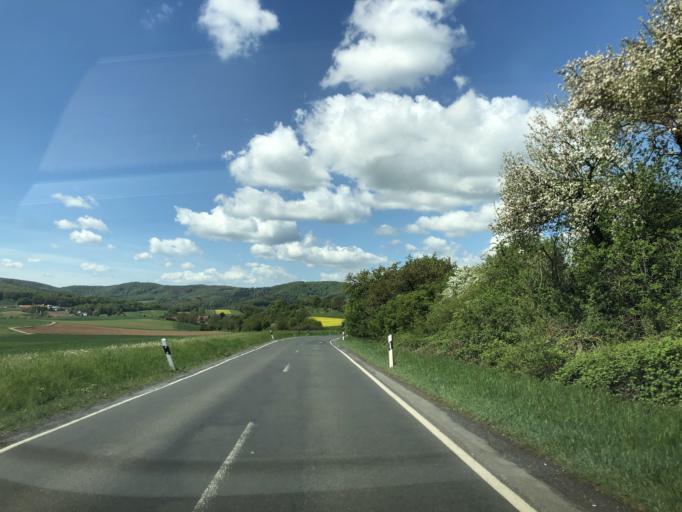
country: DE
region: Hesse
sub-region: Regierungsbezirk Kassel
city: Bad Sooden-Allendorf
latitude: 51.2688
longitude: 9.9290
